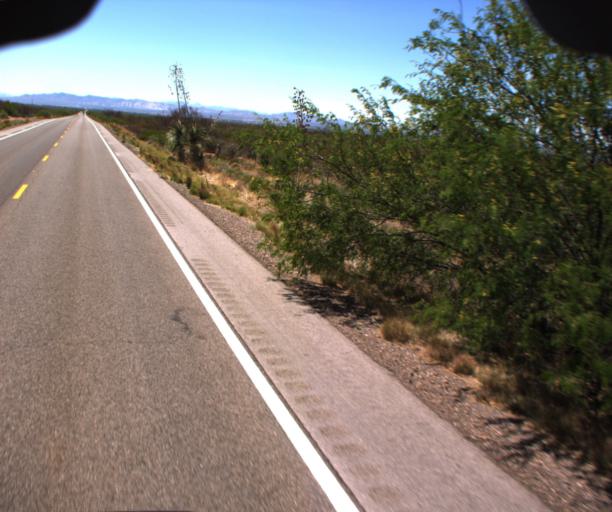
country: US
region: Arizona
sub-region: Cochise County
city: Douglas
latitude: 31.4334
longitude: -109.4817
